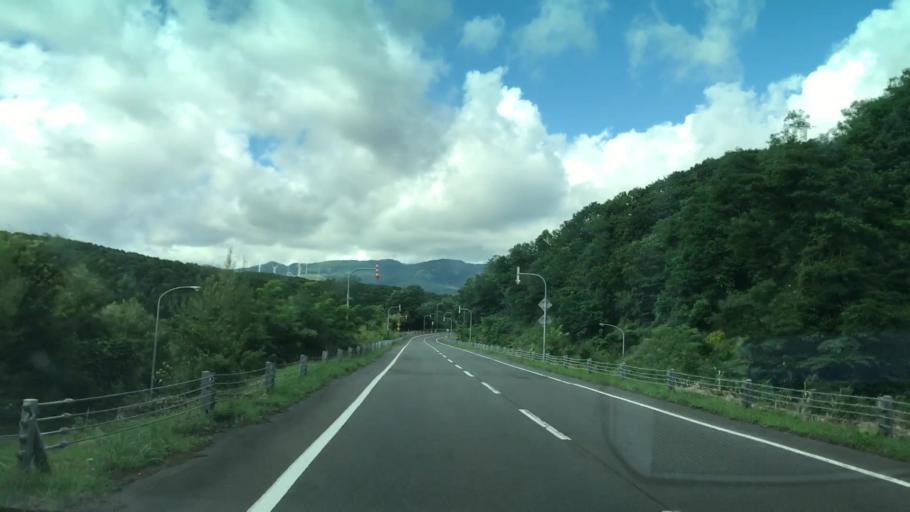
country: JP
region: Hokkaido
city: Muroran
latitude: 42.3731
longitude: 140.9614
